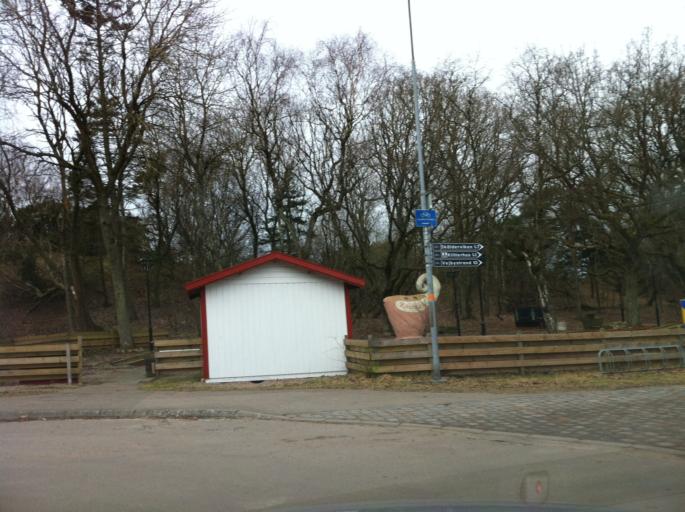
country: SE
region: Skane
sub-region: Angelholms Kommun
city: AEngelholm
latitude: 56.2543
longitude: 12.8339
